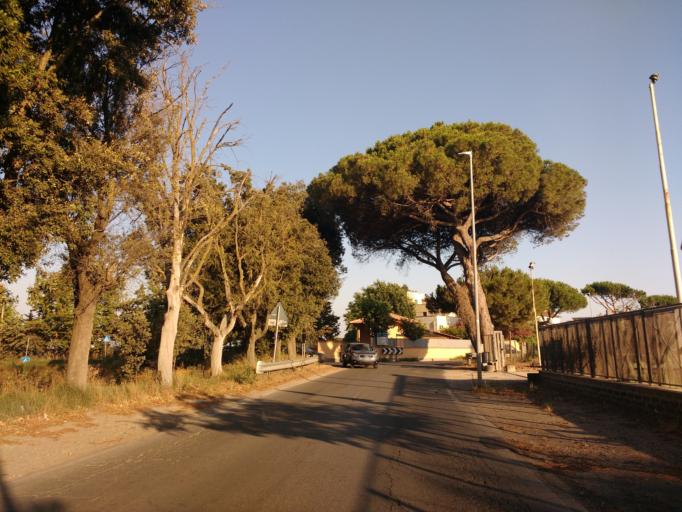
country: IT
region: Latium
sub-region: Citta metropolitana di Roma Capitale
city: Fregene
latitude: 41.8546
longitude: 12.2182
